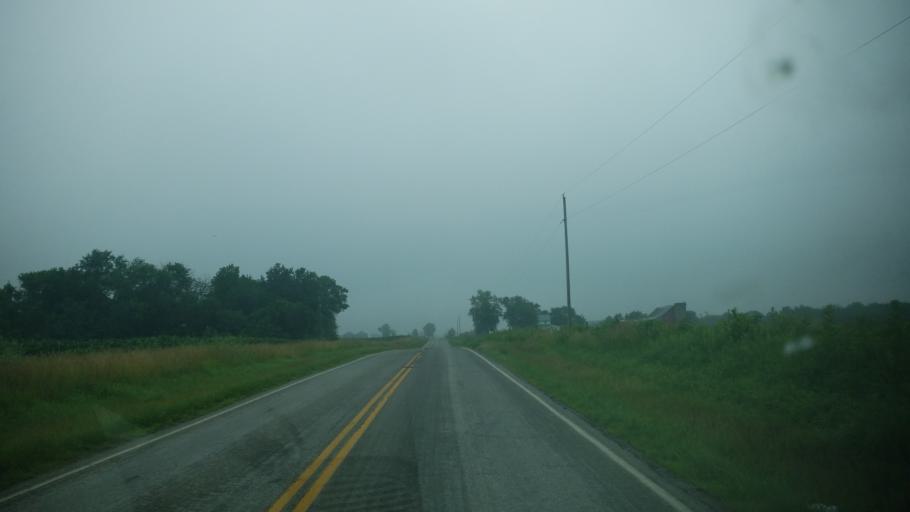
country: US
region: Missouri
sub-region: Audrain County
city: Vandalia
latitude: 39.3226
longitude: -91.3451
